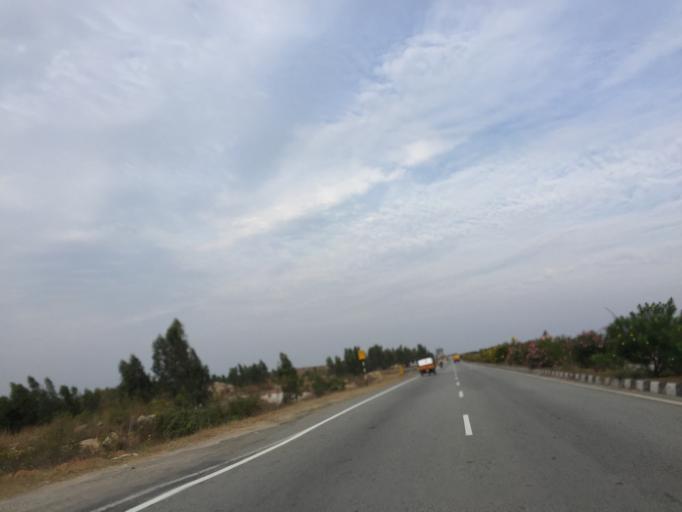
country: IN
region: Karnataka
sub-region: Kolar
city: Mulbagal
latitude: 13.1520
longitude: 78.3026
